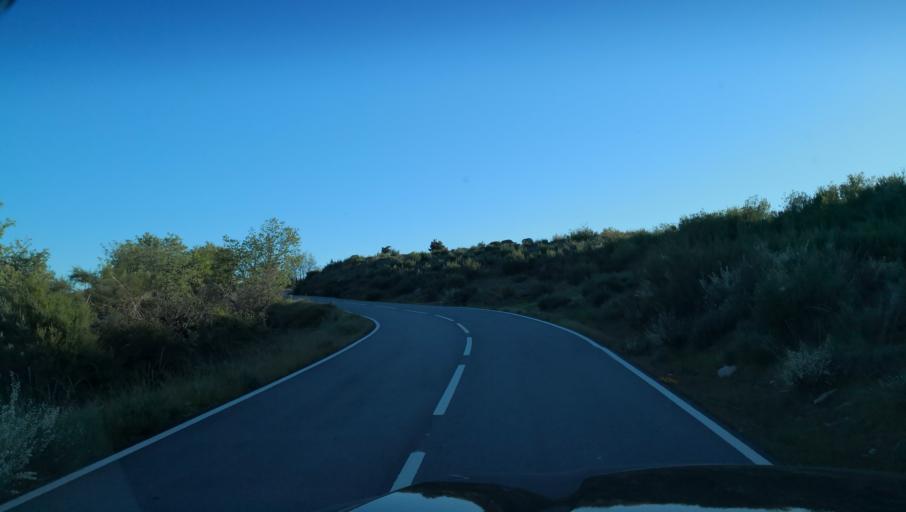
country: PT
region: Vila Real
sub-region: Sabrosa
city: Sabrosa
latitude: 41.3660
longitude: -7.6286
